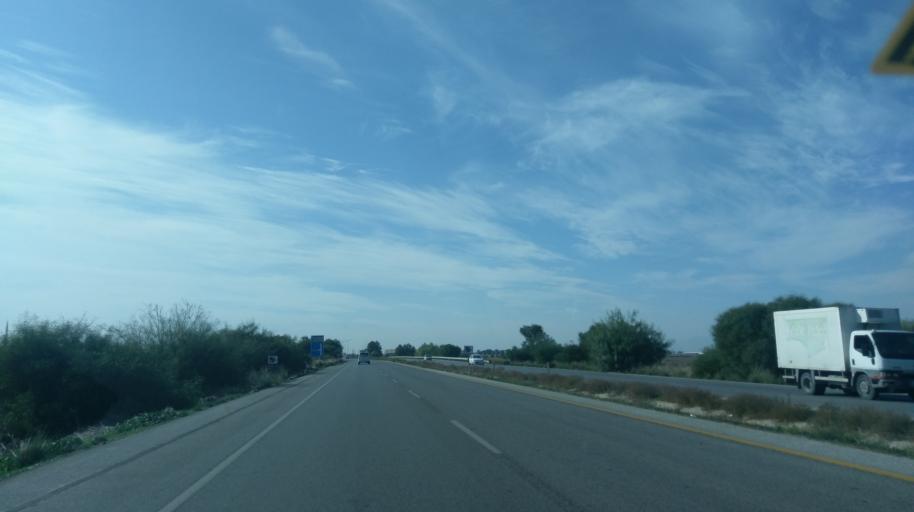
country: CY
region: Ammochostos
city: Acheritou
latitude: 35.1720
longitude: 33.7959
